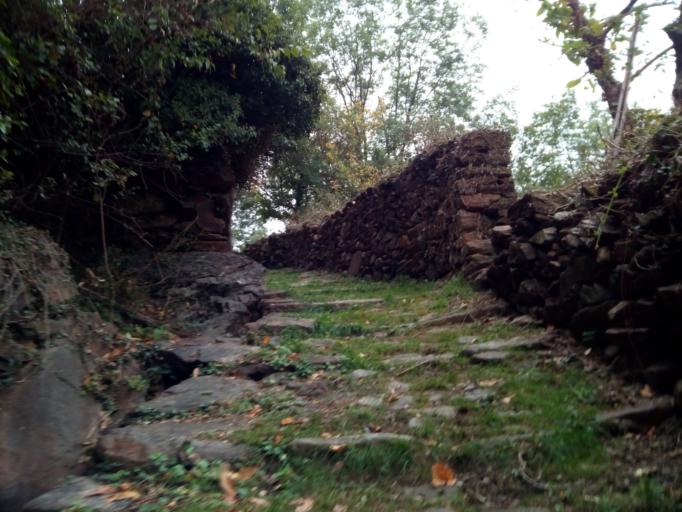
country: IT
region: Piedmont
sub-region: Provincia di Torino
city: Settimo Vittone
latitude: 45.5472
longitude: 7.8399
